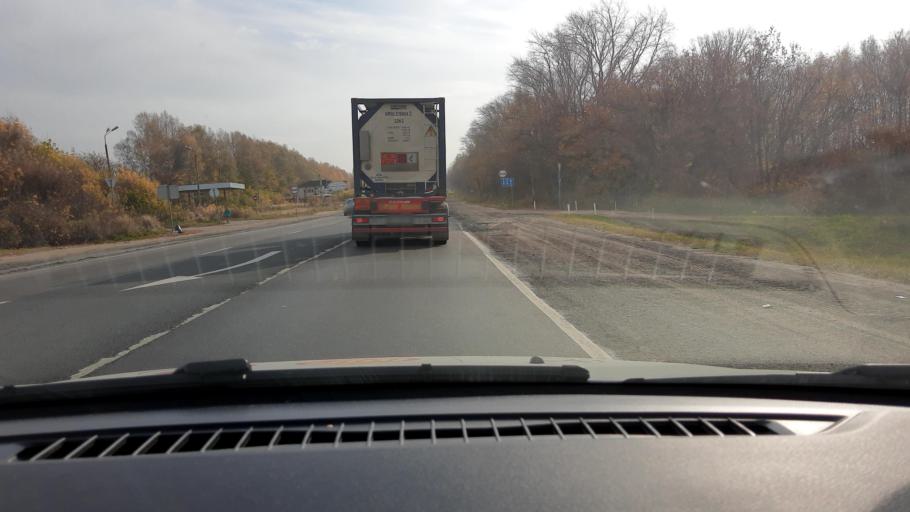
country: RU
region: Nizjnij Novgorod
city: Kstovo
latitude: 56.1187
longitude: 44.2745
